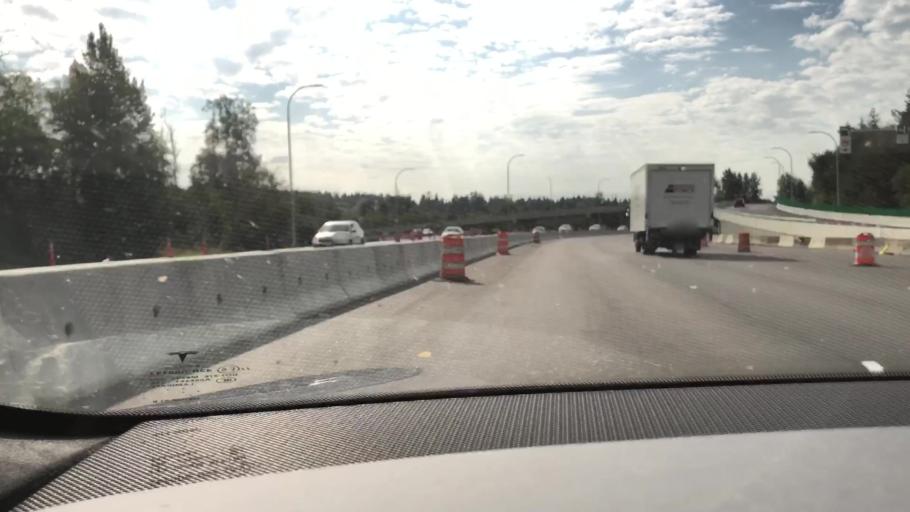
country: CA
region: British Columbia
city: Delta
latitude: 49.1355
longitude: -122.9300
